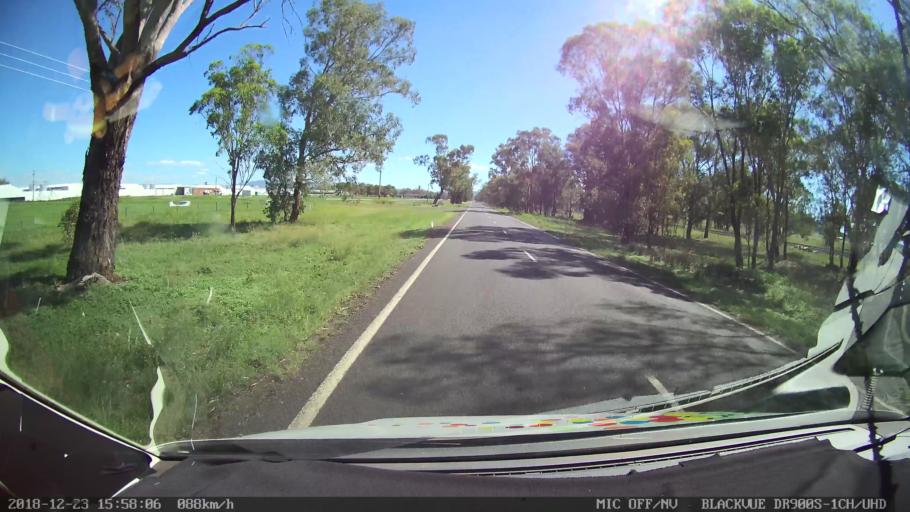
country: AU
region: New South Wales
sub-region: Tamworth Municipality
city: Phillip
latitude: -31.1844
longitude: 150.8445
